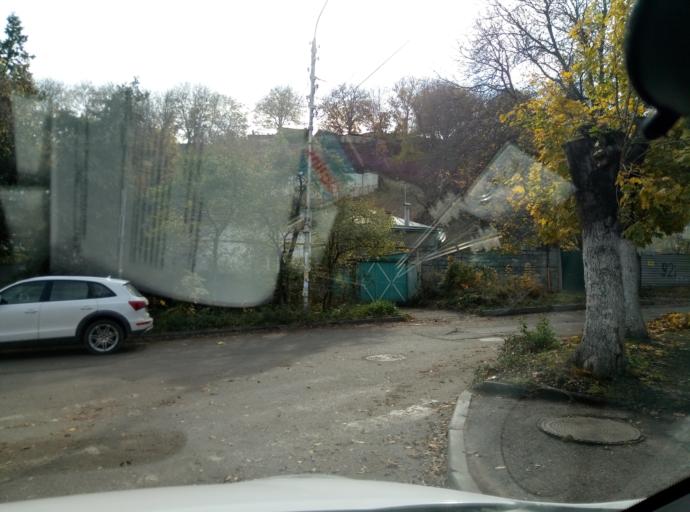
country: RU
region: Stavropol'skiy
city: Kislovodsk
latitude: 43.9060
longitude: 42.7081
